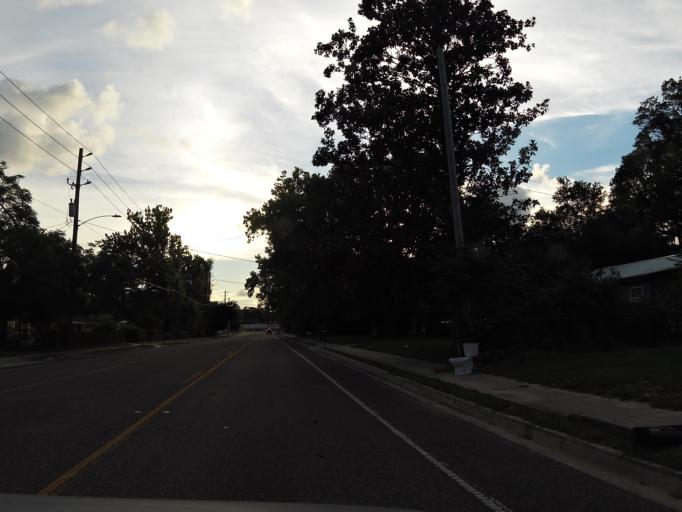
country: US
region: Florida
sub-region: Duval County
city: Jacksonville
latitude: 30.4298
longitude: -81.6907
